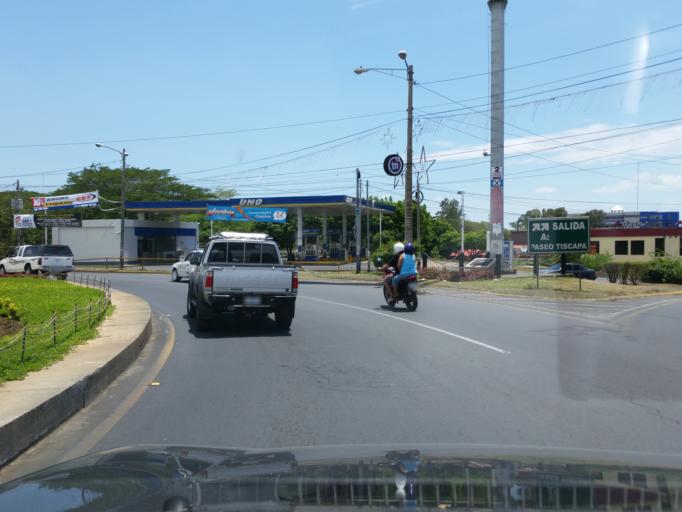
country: NI
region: Managua
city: Managua
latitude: 12.1295
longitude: -86.2662
